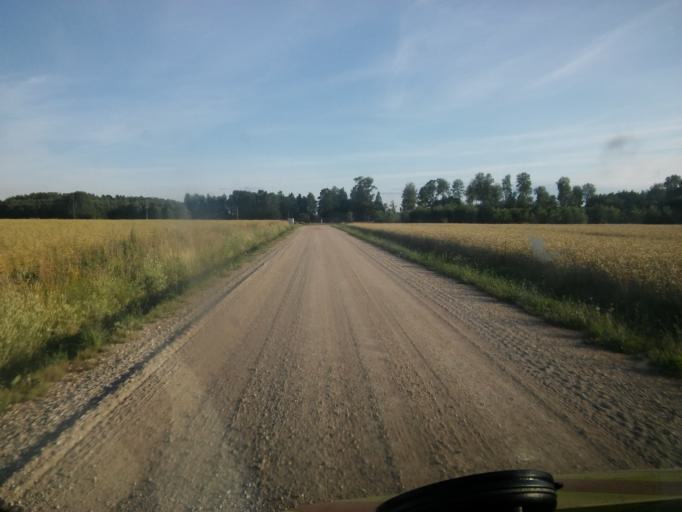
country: EE
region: Valgamaa
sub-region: Torva linn
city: Torva
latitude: 58.0502
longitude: 25.9171
